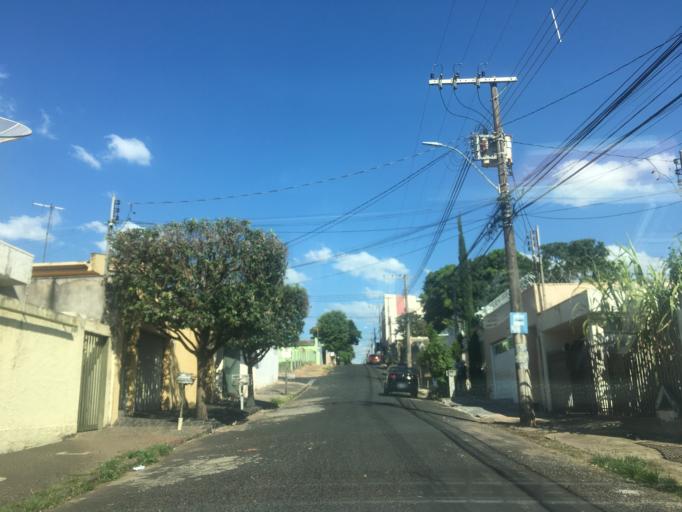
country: BR
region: Minas Gerais
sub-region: Uberlandia
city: Uberlandia
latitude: -18.9057
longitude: -48.2825
